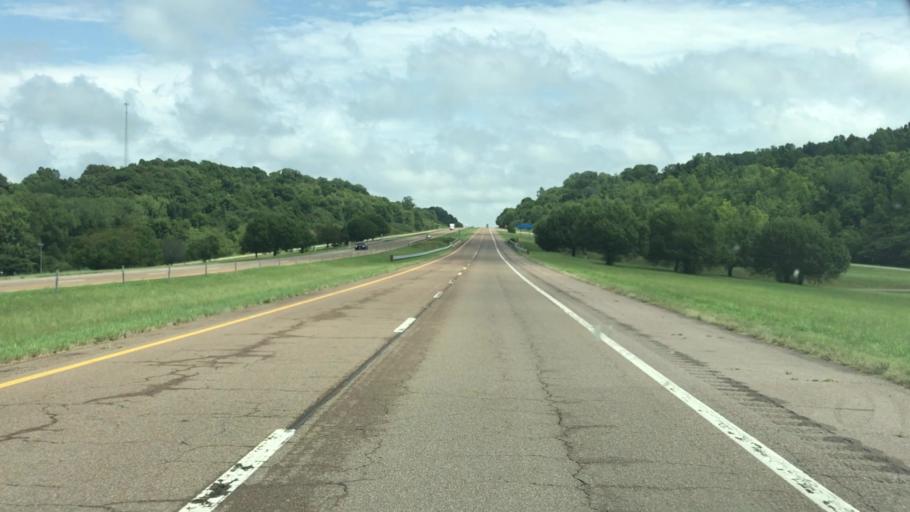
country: US
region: Tennessee
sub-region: Dyer County
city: Dyersburg
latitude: 36.0757
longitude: -89.4992
